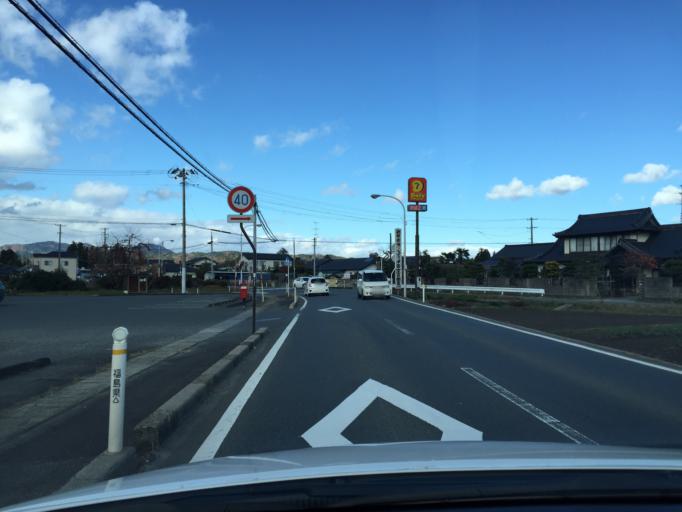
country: JP
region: Fukushima
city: Namie
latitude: 37.6562
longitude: 140.9402
